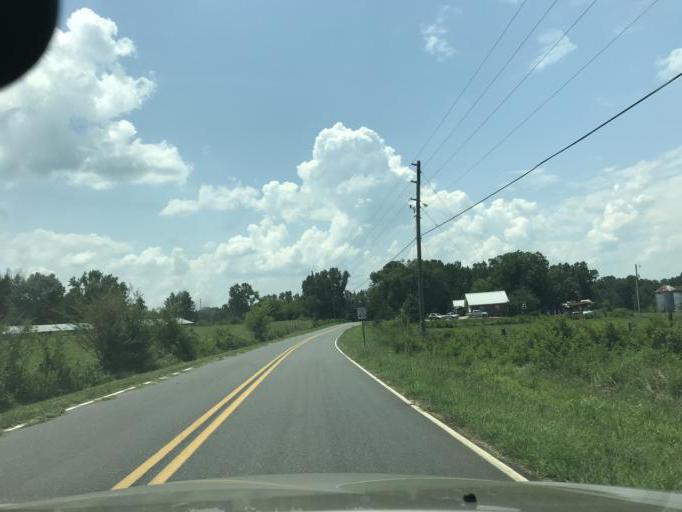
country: US
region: Georgia
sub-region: Dawson County
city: Dawsonville
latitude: 34.3339
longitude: -84.1490
